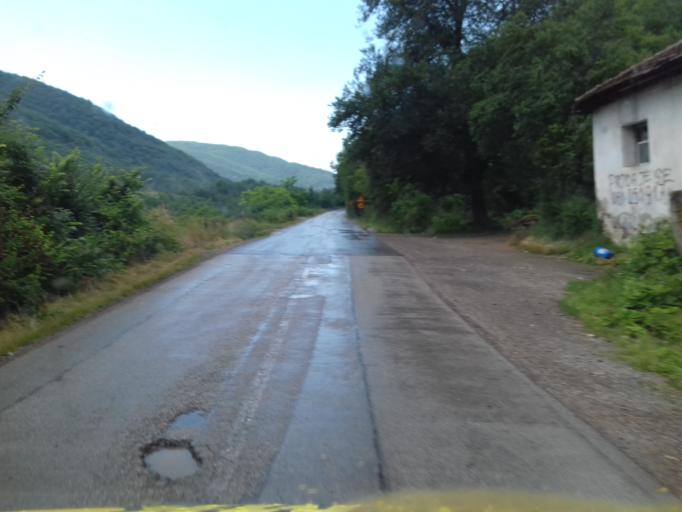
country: BA
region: Federation of Bosnia and Herzegovina
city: Visoko
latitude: 43.9551
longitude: 18.1521
